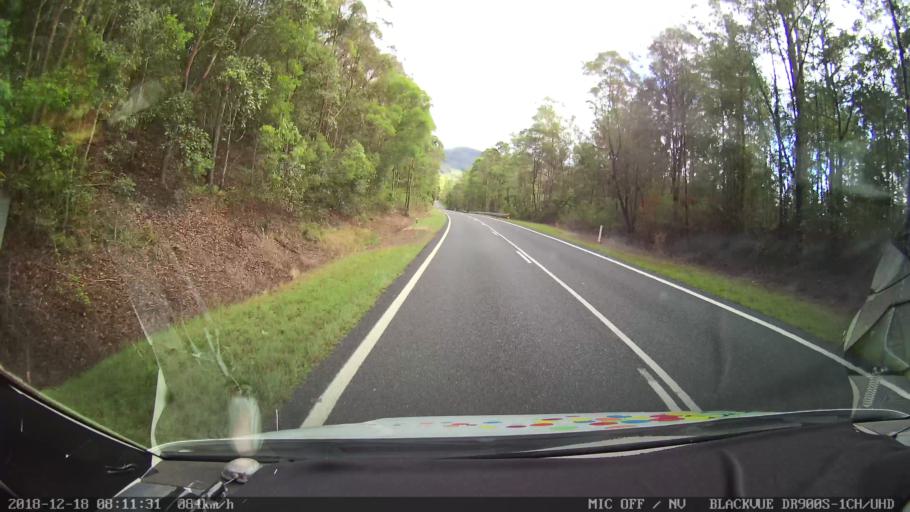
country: AU
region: New South Wales
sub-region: Kyogle
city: Kyogle
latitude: -28.3500
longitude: 152.6692
